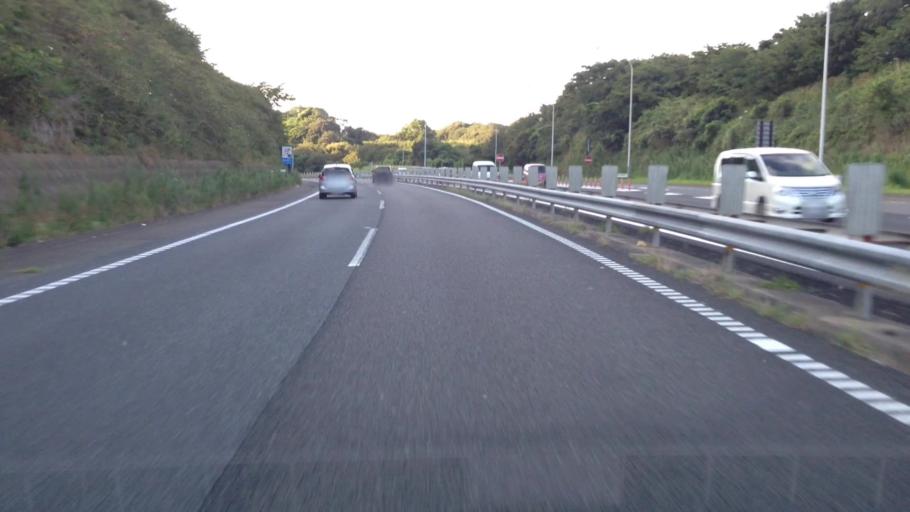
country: JP
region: Kanagawa
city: Yokosuka
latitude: 35.2731
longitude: 139.6348
